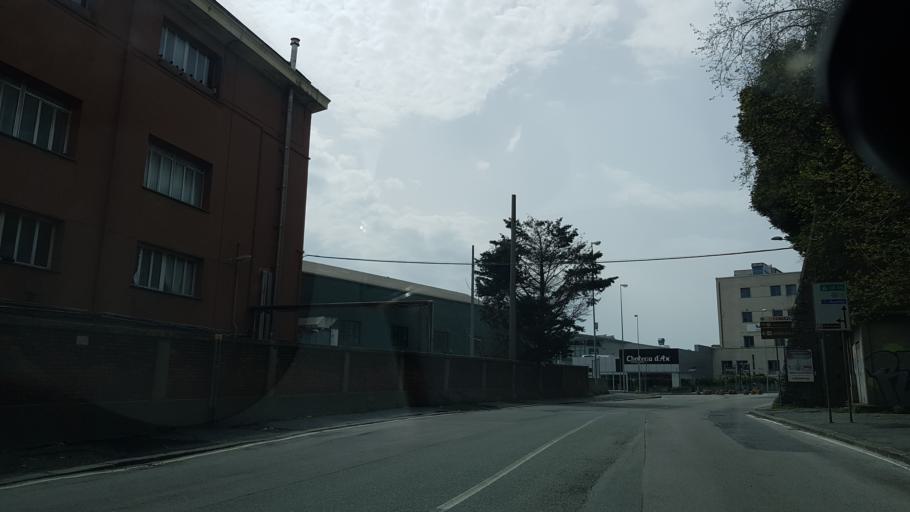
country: IT
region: Liguria
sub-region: Provincia di Genova
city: San Teodoro
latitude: 44.4250
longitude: 8.8827
